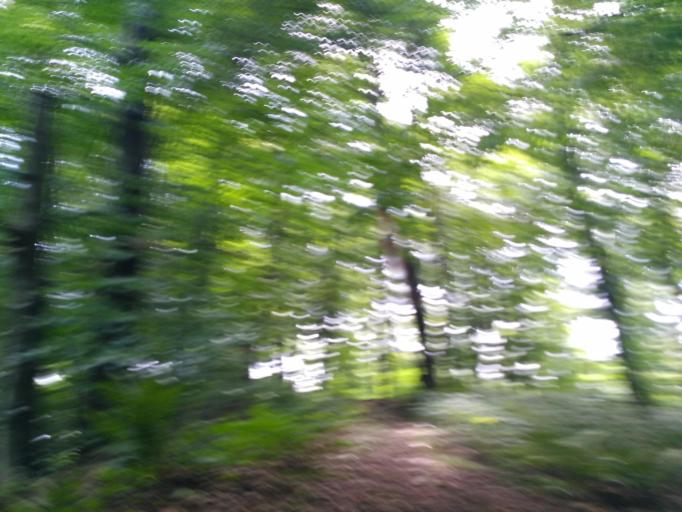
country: PL
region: Subcarpathian Voivodeship
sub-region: Powiat strzyzowski
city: Frysztak
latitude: 49.8886
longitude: 21.5386
